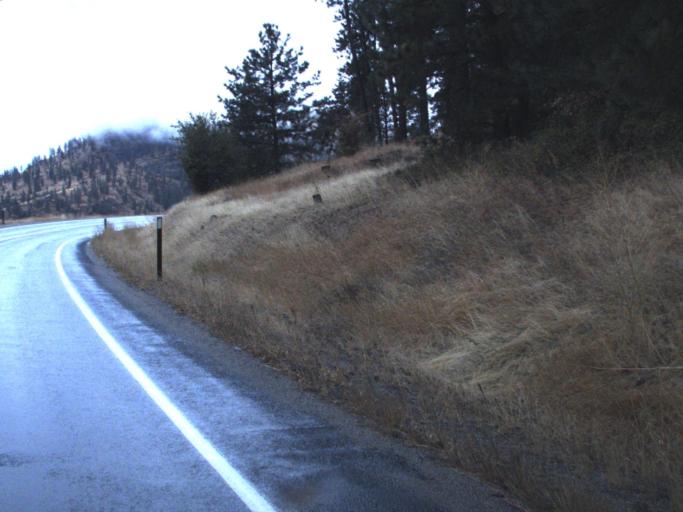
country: US
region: Washington
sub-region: Stevens County
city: Chewelah
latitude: 48.1947
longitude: -117.7426
